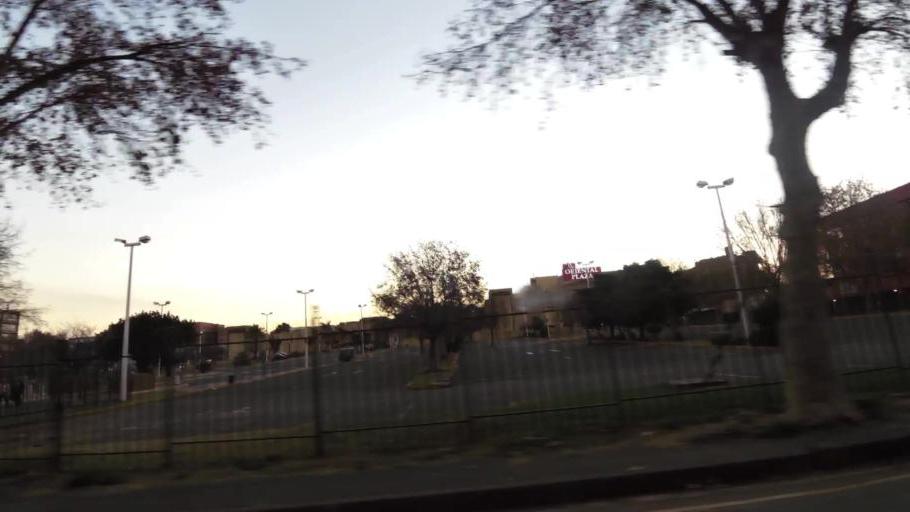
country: ZA
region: Gauteng
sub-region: City of Johannesburg Metropolitan Municipality
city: Johannesburg
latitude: -26.2051
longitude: 28.0266
